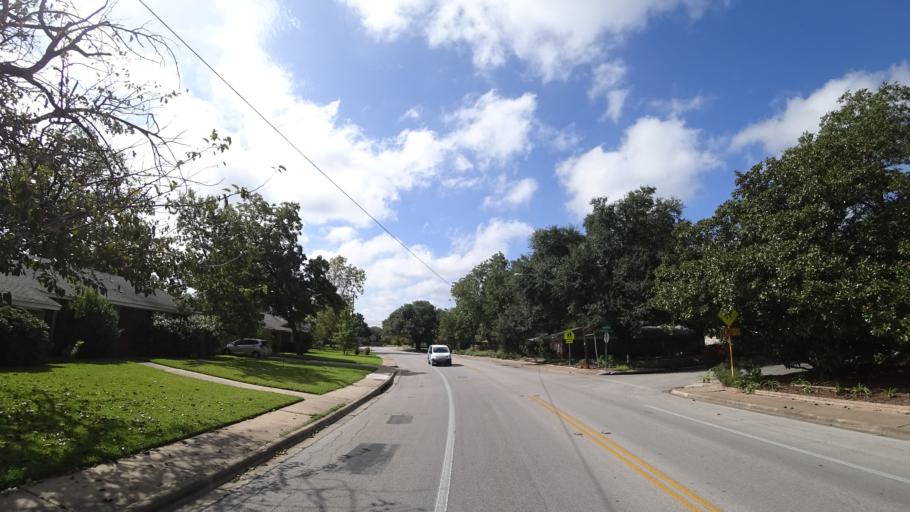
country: US
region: Texas
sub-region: Travis County
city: West Lake Hills
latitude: 30.3524
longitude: -97.7417
